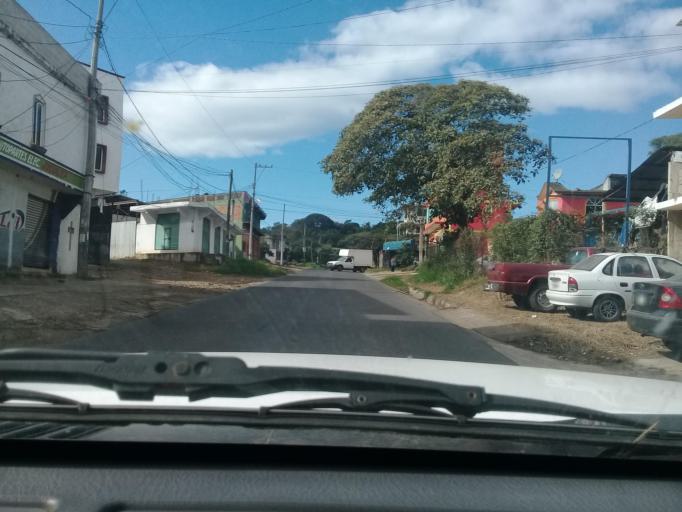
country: MX
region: Veracruz
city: El Castillo
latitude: 19.5478
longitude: -96.8816
